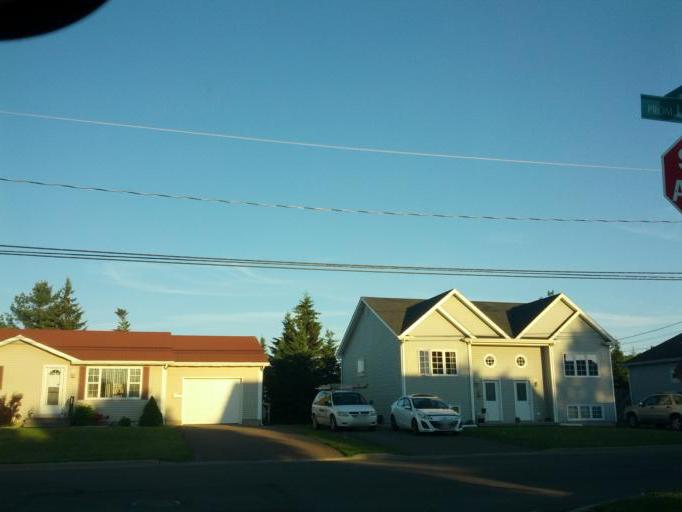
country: CA
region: New Brunswick
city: Moncton
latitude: 46.1189
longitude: -64.8506
